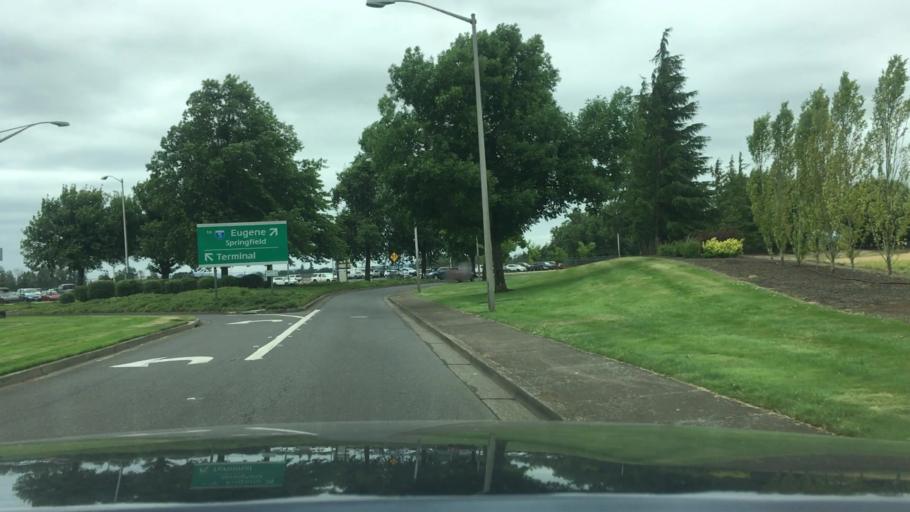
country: US
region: Oregon
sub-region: Lane County
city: Junction City
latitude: 44.1161
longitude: -123.2094
